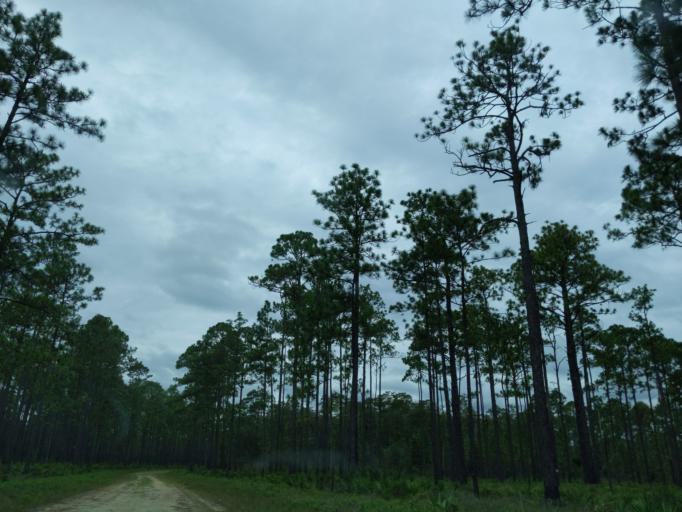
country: US
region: Florida
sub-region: Gadsden County
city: Midway
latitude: 30.3651
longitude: -84.4823
